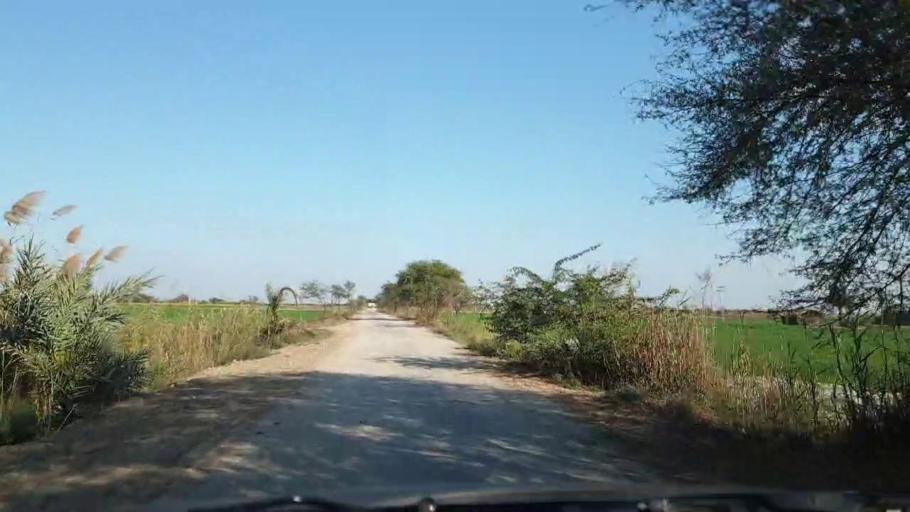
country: PK
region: Sindh
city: Khadro
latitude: 26.1899
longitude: 68.7602
